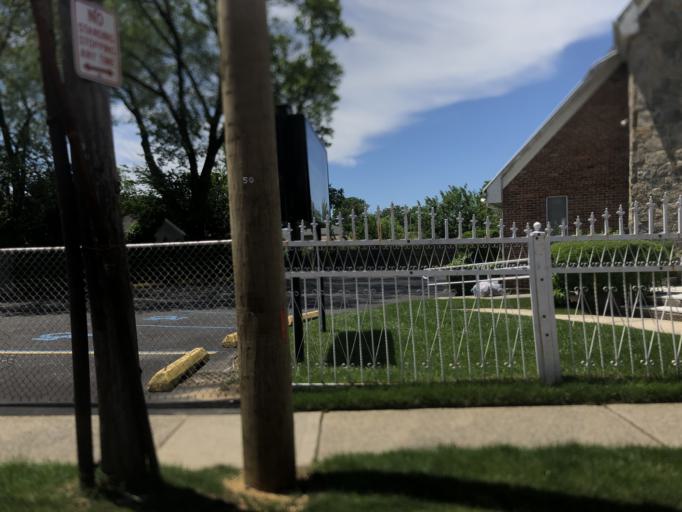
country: US
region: New York
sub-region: Nassau County
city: Freeport
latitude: 40.6677
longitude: -73.5745
